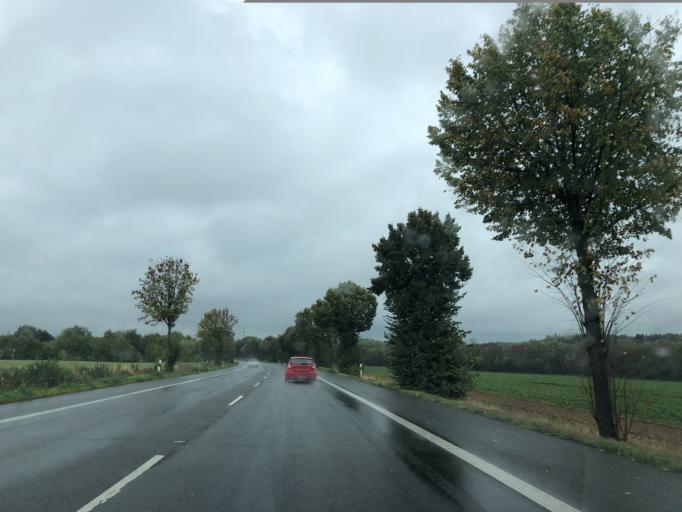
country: DE
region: North Rhine-Westphalia
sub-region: Regierungsbezirk Dusseldorf
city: Grevenbroich
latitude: 51.0659
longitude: 6.5573
